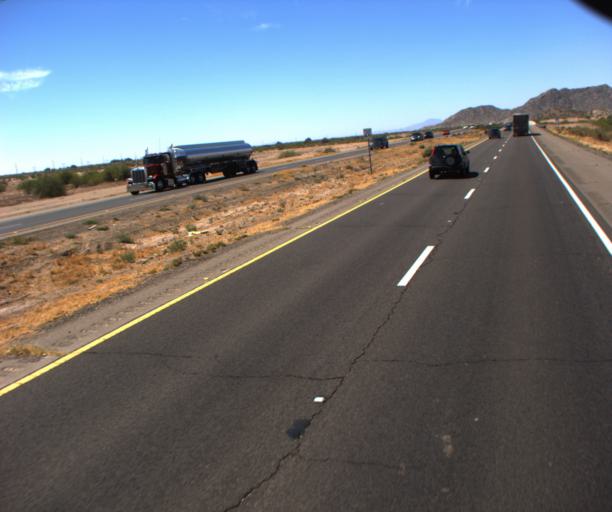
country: US
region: Arizona
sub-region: Pinal County
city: Maricopa
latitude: 33.1763
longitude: -112.0036
